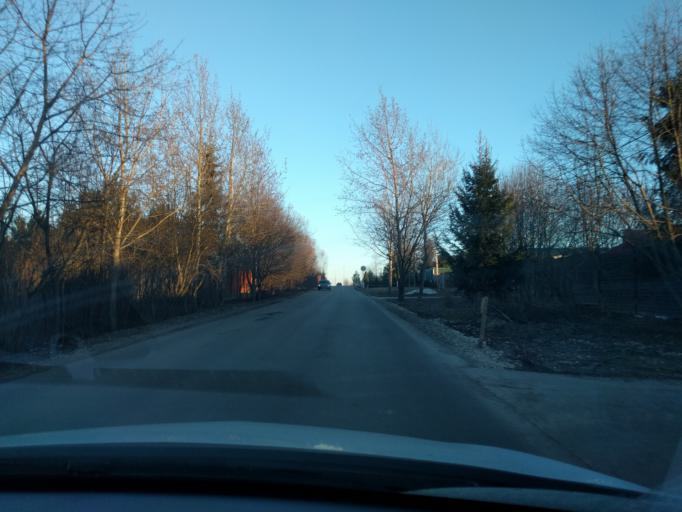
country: RU
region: Moskovskaya
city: Dubrovitsy
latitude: 55.4906
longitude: 37.4310
